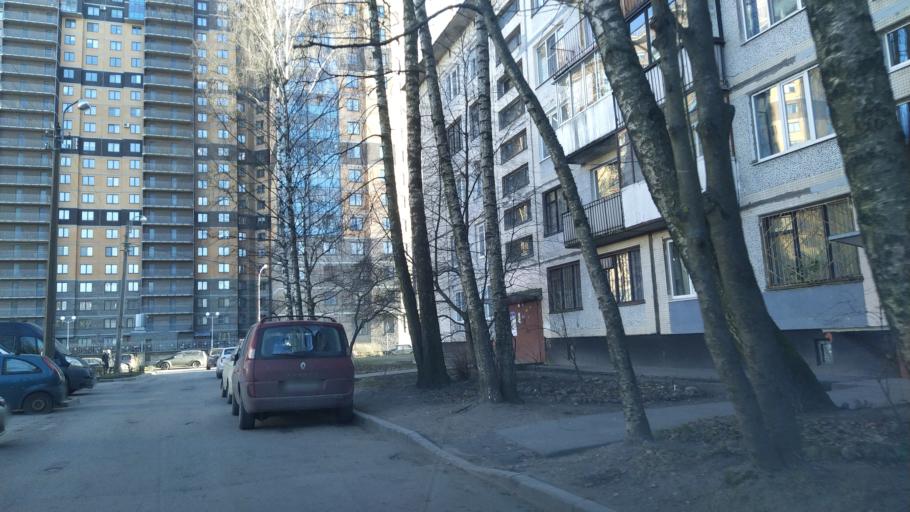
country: RU
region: St.-Petersburg
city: Grazhdanka
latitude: 60.0403
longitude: 30.4060
